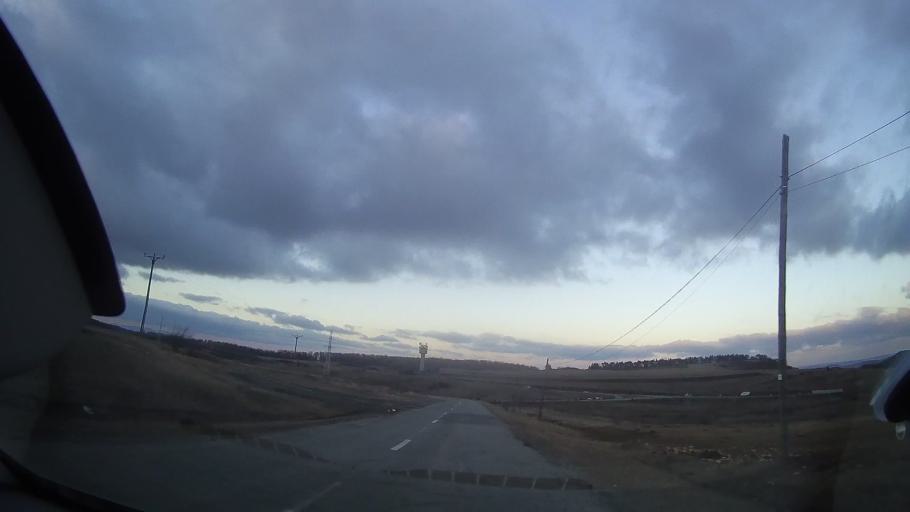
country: RO
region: Cluj
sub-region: Comuna Izvoru Crisului
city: Izvoru Crisului
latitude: 46.8218
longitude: 23.1533
